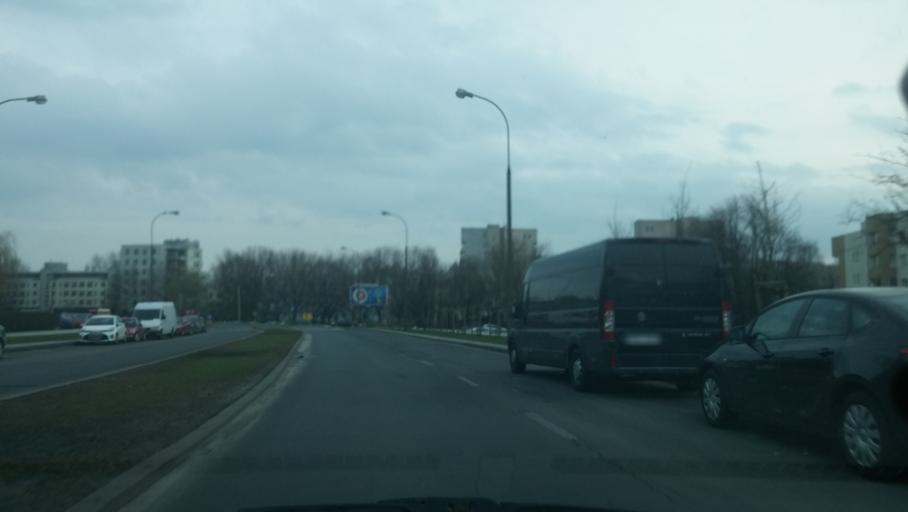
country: PL
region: Masovian Voivodeship
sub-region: Warszawa
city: Praga Poludnie
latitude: 52.2247
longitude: 21.0838
